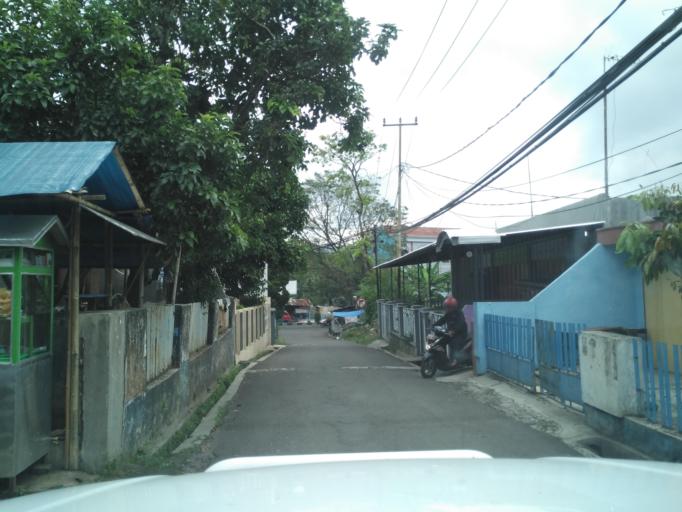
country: ID
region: West Java
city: Ciranjang-hilir
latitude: -6.8136
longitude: 107.1395
